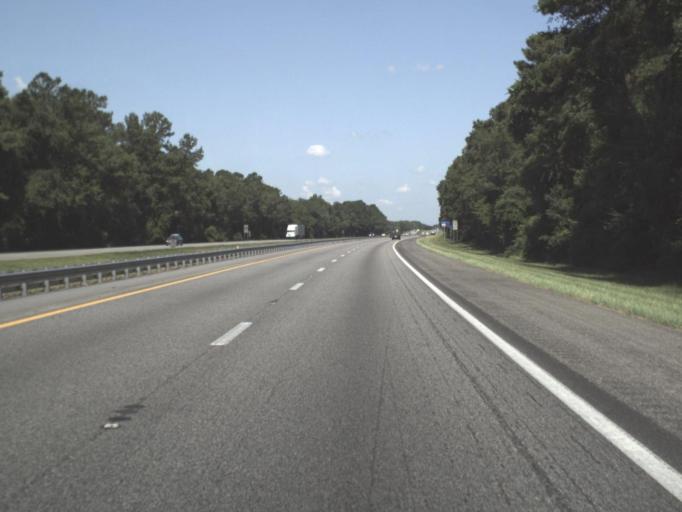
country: US
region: Florida
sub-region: Madison County
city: Madison
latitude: 30.4318
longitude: -83.6115
